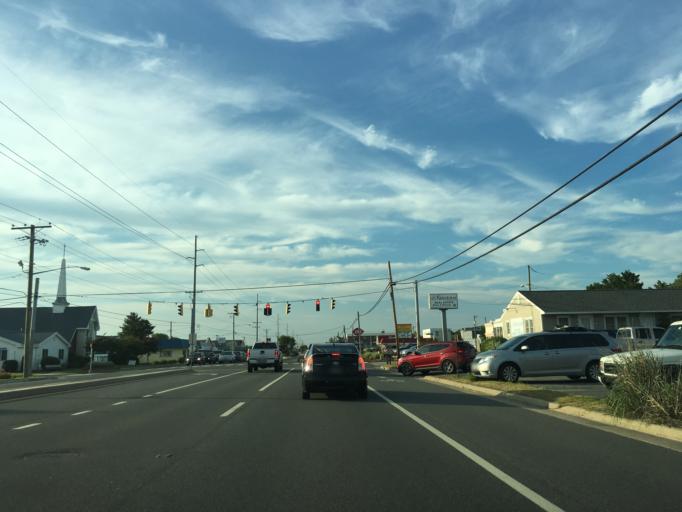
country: US
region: Delaware
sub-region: Sussex County
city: Bethany Beach
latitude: 38.4589
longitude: -75.0520
